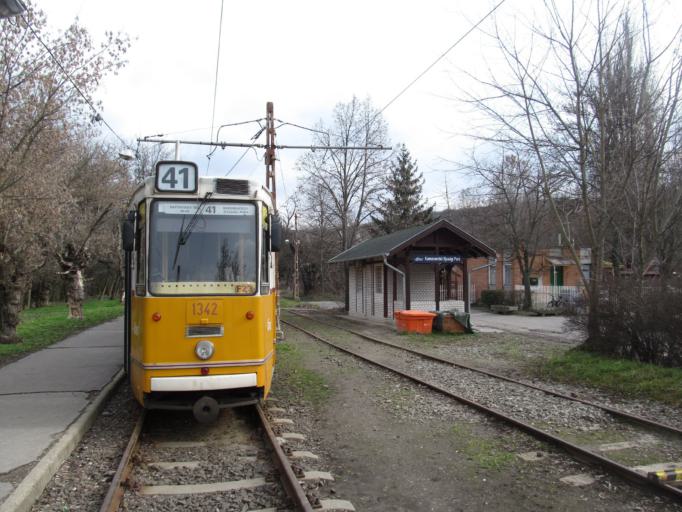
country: HU
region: Pest
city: Budaors
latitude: 47.4411
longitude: 18.9795
